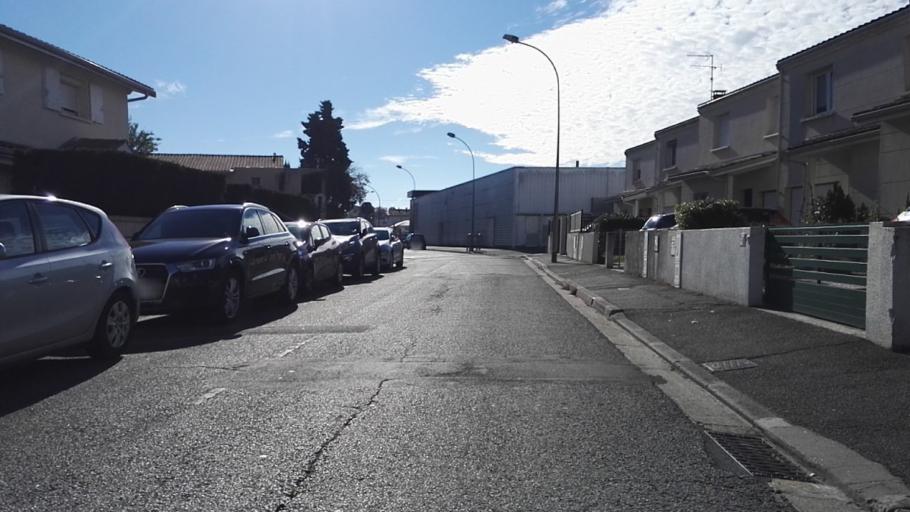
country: FR
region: Aquitaine
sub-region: Departement de la Gironde
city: Eysines
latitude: 44.8617
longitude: -0.6333
